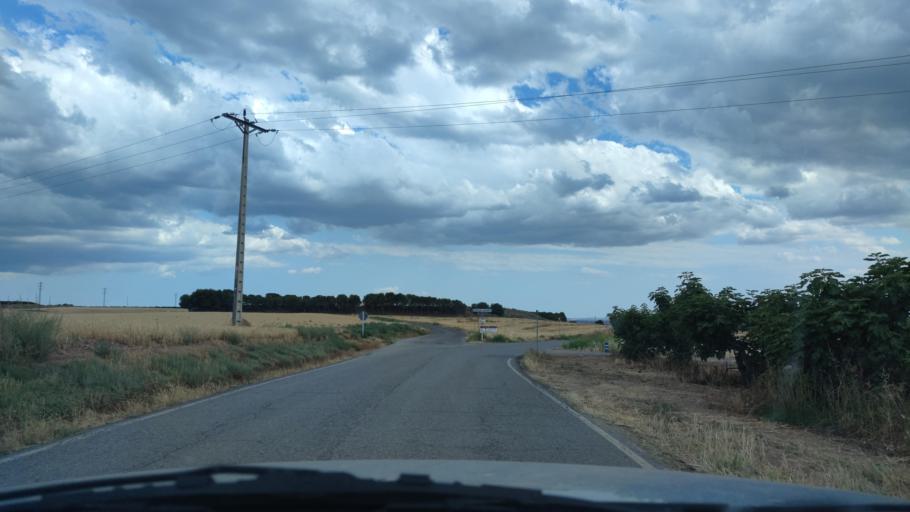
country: ES
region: Catalonia
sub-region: Provincia de Lleida
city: Lleida
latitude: 41.6081
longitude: 0.5846
